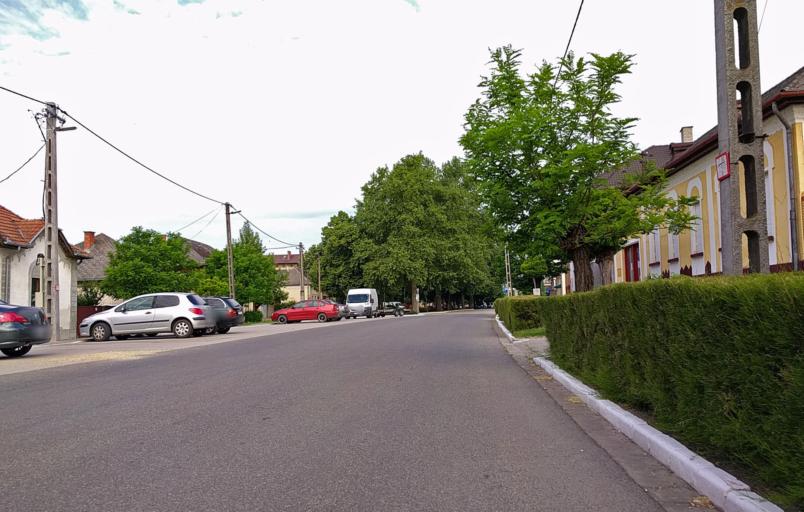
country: HU
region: Bacs-Kiskun
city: Tiszakecske
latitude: 46.9303
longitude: 20.0977
